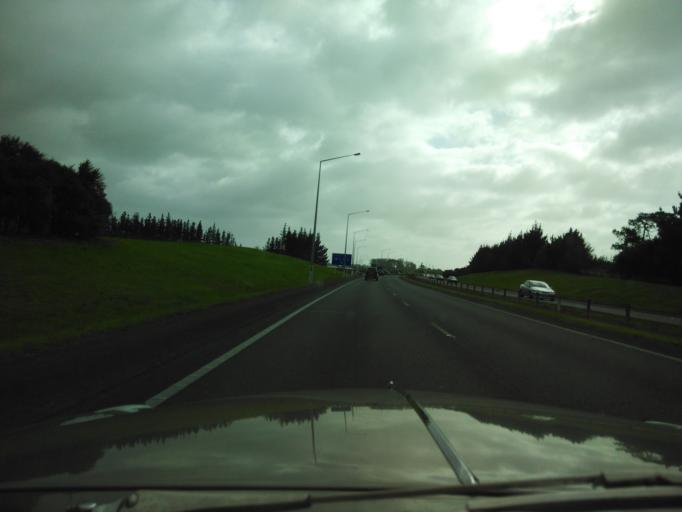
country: NZ
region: Auckland
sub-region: Auckland
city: Rothesay Bay
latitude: -36.6632
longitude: 174.6717
